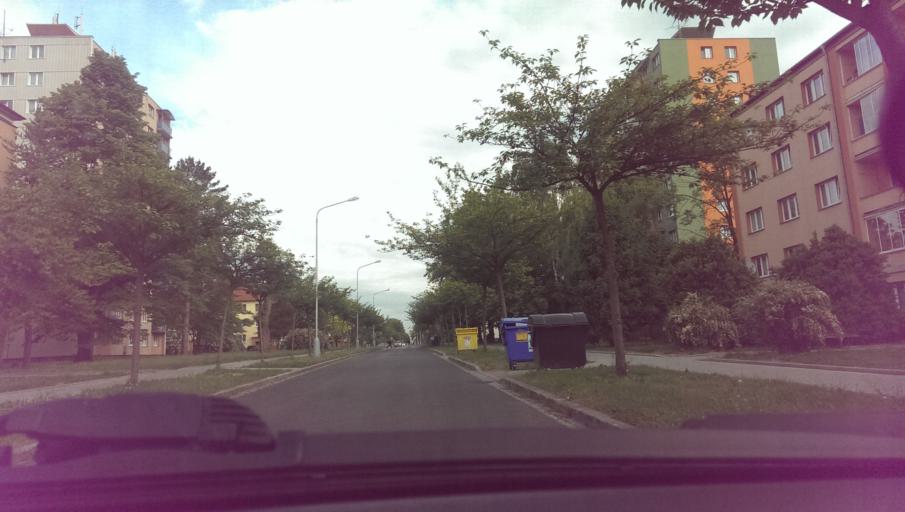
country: CZ
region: Zlin
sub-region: Okres Kromeriz
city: Kromeriz
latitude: 49.2889
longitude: 17.3942
